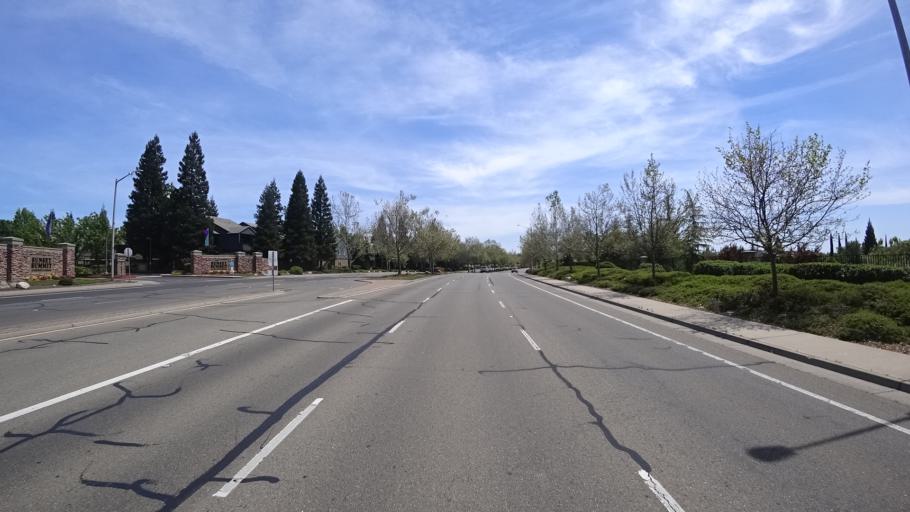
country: US
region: California
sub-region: Placer County
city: Rocklin
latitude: 38.8072
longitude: -121.2763
